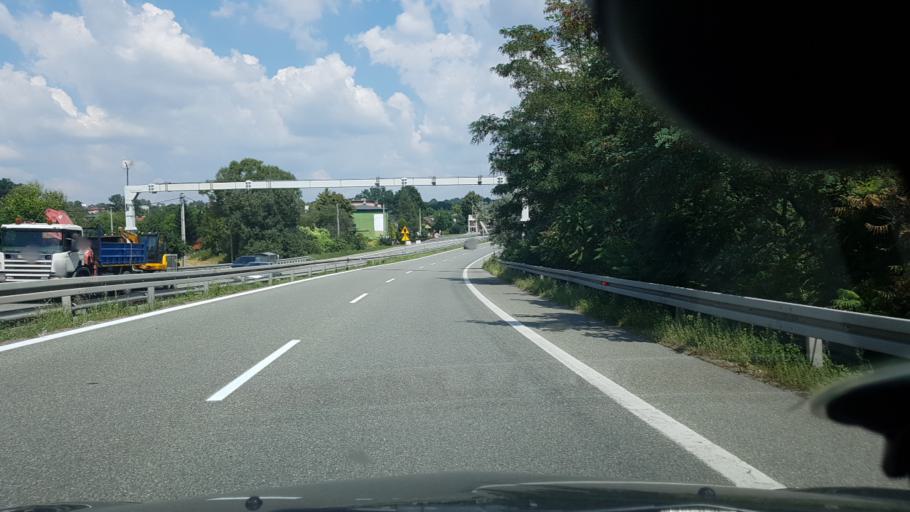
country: PL
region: Silesian Voivodeship
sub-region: Powiat mikolowski
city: Laziska Gorne
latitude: 50.1351
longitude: 18.8304
